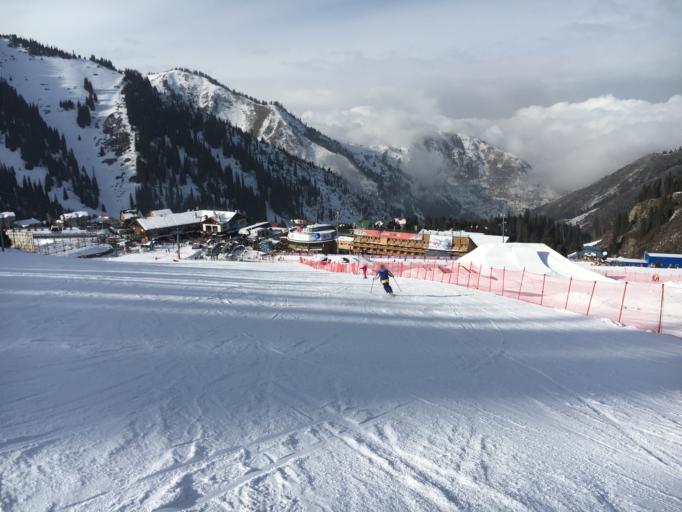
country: KZ
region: Almaty Qalasy
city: Almaty
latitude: 43.1266
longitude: 77.0850
